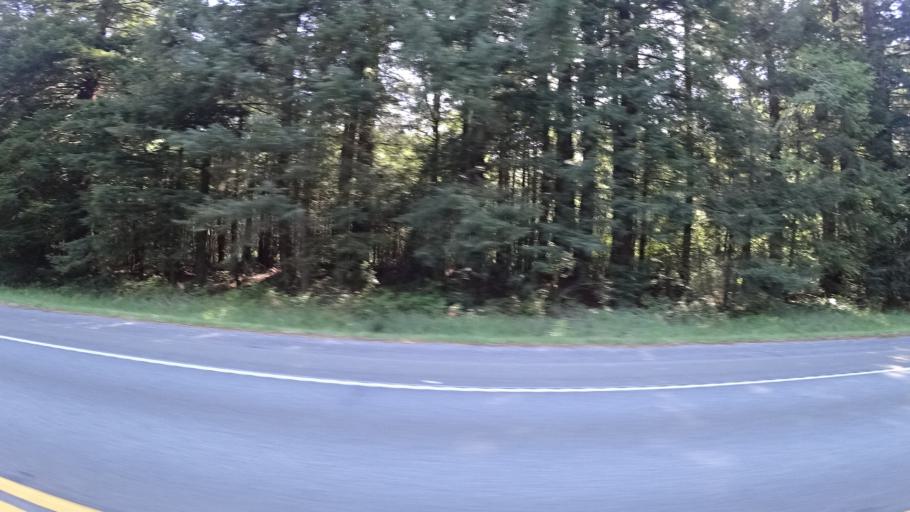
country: US
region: California
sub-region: Del Norte County
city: Bertsch-Oceanview
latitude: 41.8121
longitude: -124.1468
